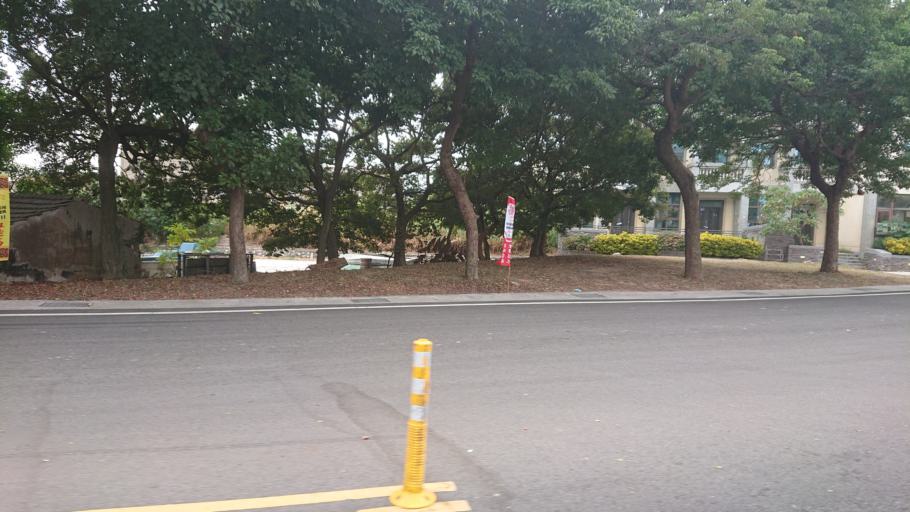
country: TW
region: Fukien
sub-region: Kinmen
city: Jincheng
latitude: 24.4170
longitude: 118.3082
